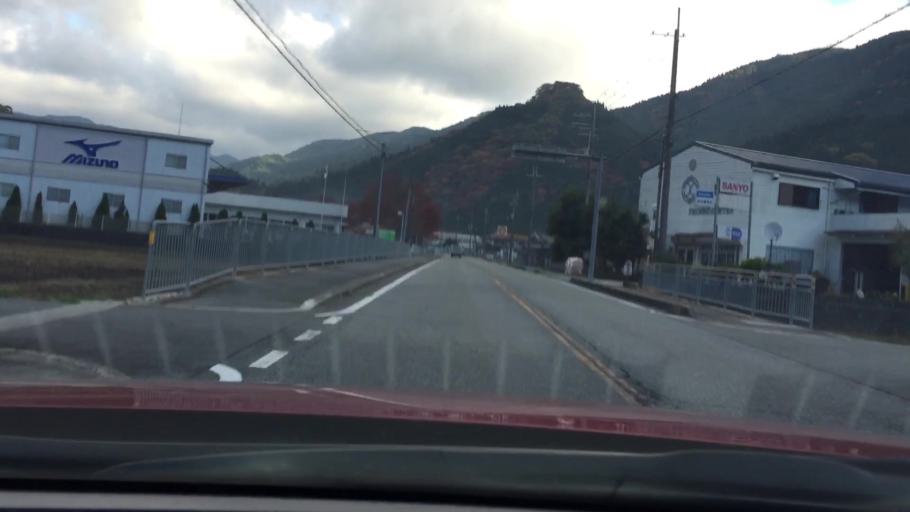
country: JP
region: Hyogo
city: Yamazakicho-nakabirose
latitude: 35.1521
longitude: 134.5427
